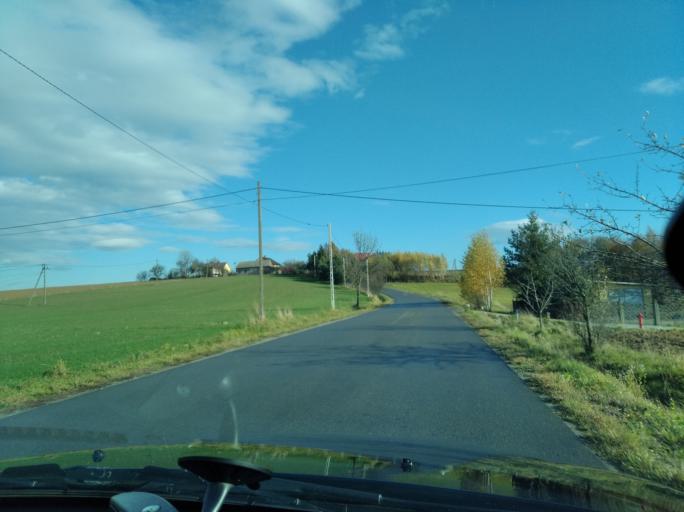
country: PL
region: Subcarpathian Voivodeship
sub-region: Powiat ropczycko-sedziszowski
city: Niedzwiada
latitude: 50.0062
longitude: 21.4713
